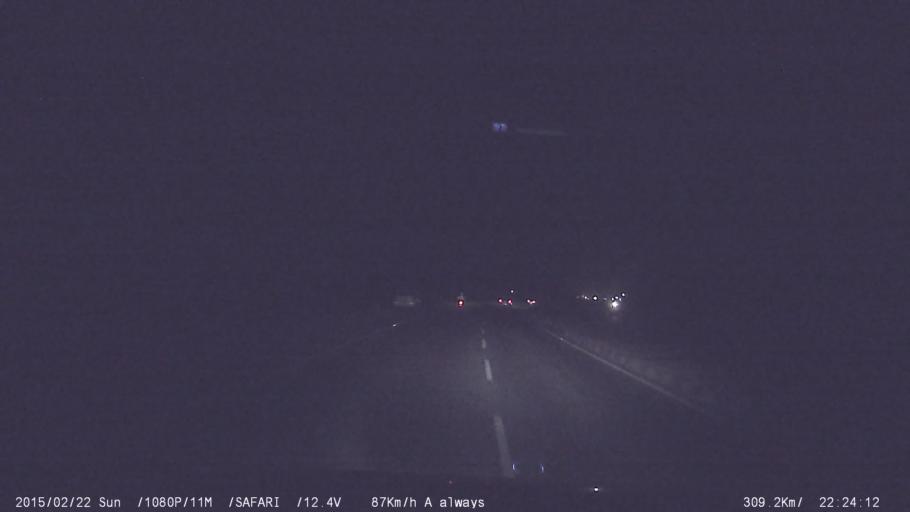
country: IN
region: Tamil Nadu
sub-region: Karur
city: Karur
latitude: 11.0344
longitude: 78.0621
